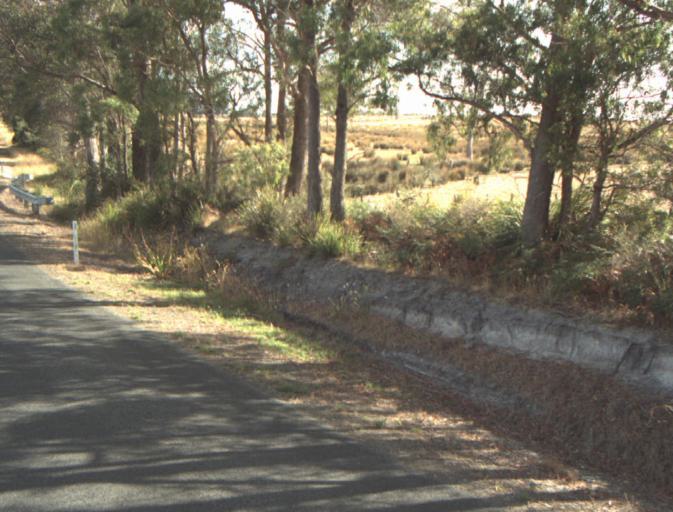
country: AU
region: Tasmania
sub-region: Dorset
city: Bridport
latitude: -41.1128
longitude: 147.2005
